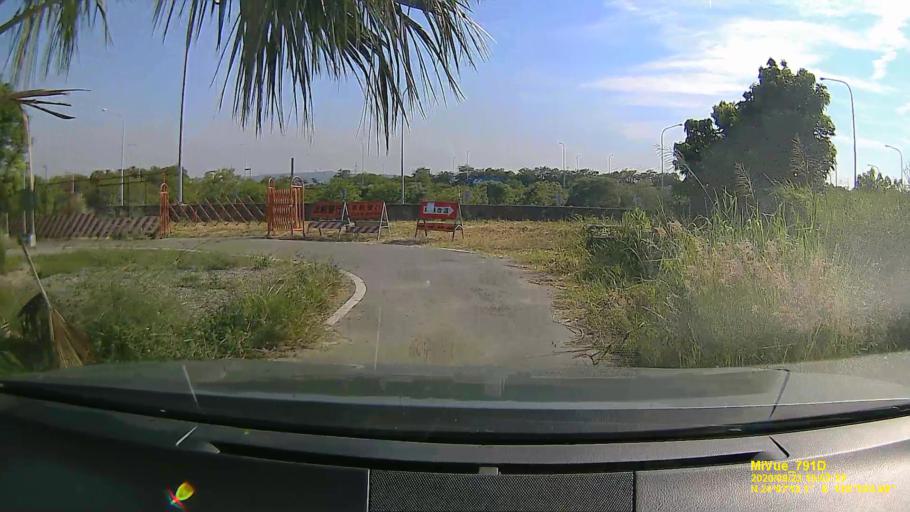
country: TW
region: Taiwan
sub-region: Changhua
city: Chang-hua
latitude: 24.1203
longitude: 120.5847
